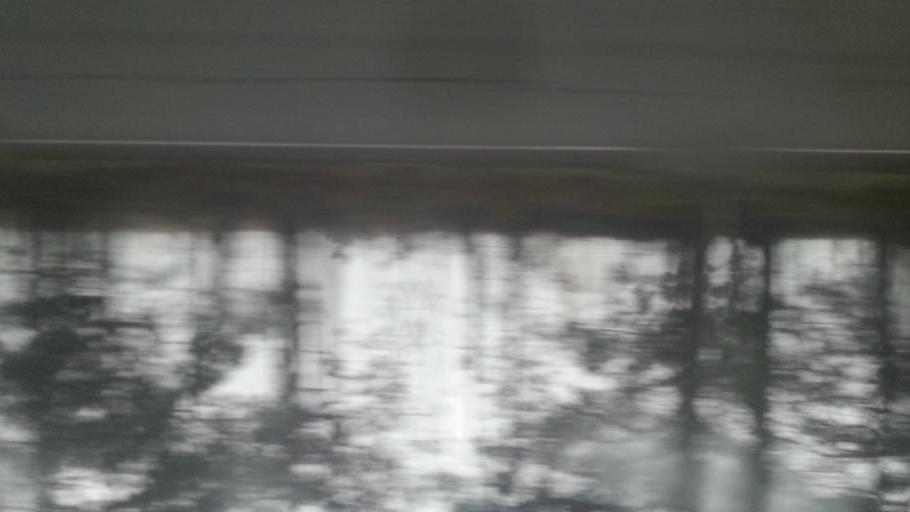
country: AU
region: New South Wales
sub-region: Wollondilly
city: Douglas Park
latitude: -34.2396
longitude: 150.7284
